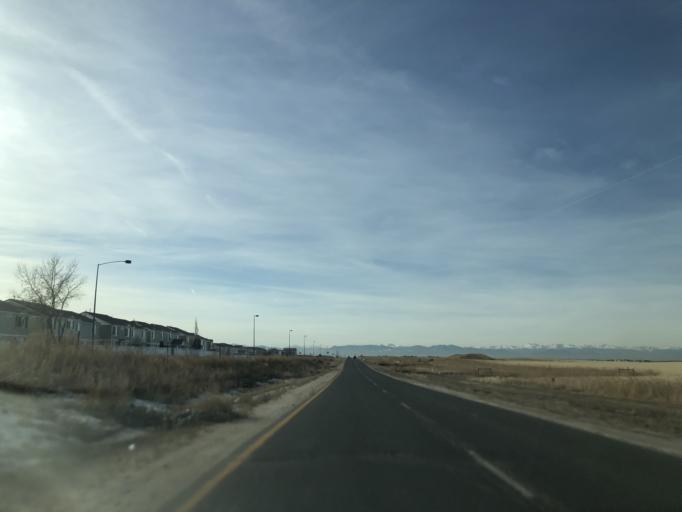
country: US
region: Colorado
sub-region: Adams County
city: Aurora
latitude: 39.7984
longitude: -104.7358
